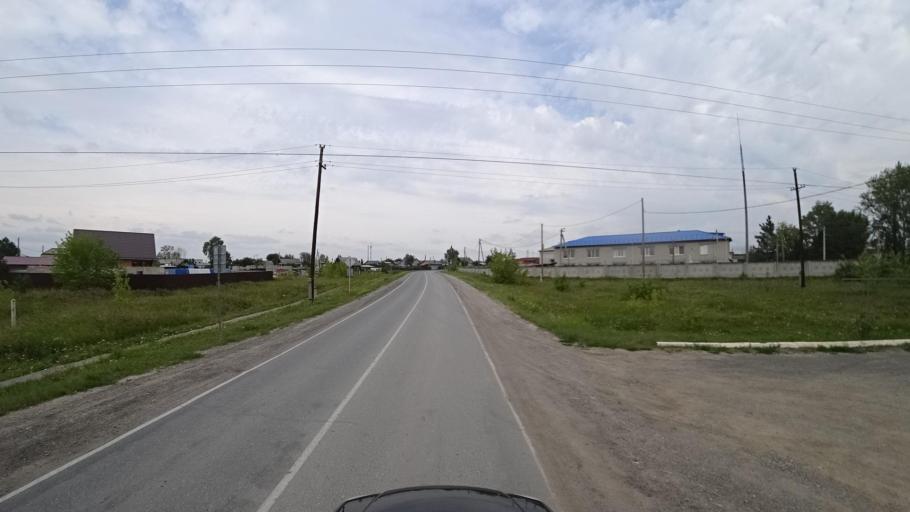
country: RU
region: Sverdlovsk
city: Kamyshlov
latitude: 56.8482
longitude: 62.7434
